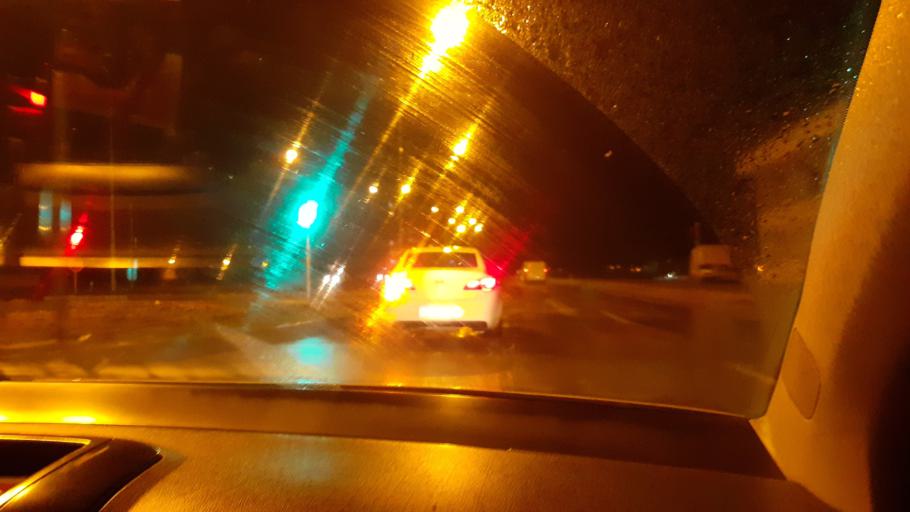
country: TR
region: Hatay
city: Hassa
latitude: 36.7976
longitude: 36.5335
